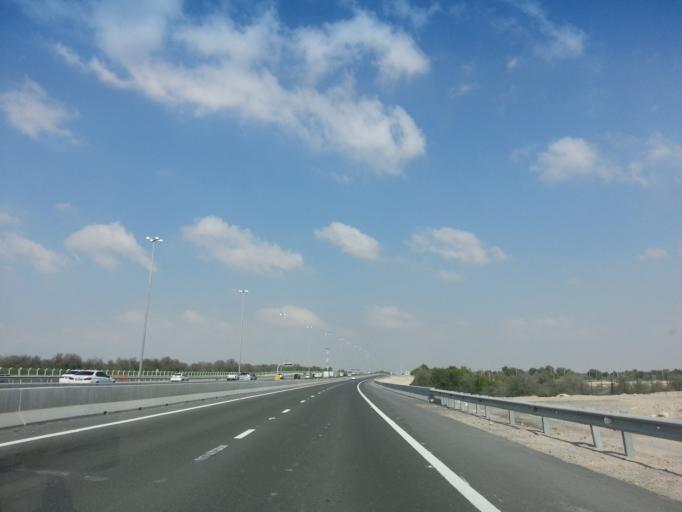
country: AE
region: Abu Dhabi
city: Abu Dhabi
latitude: 24.7016
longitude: 54.7855
